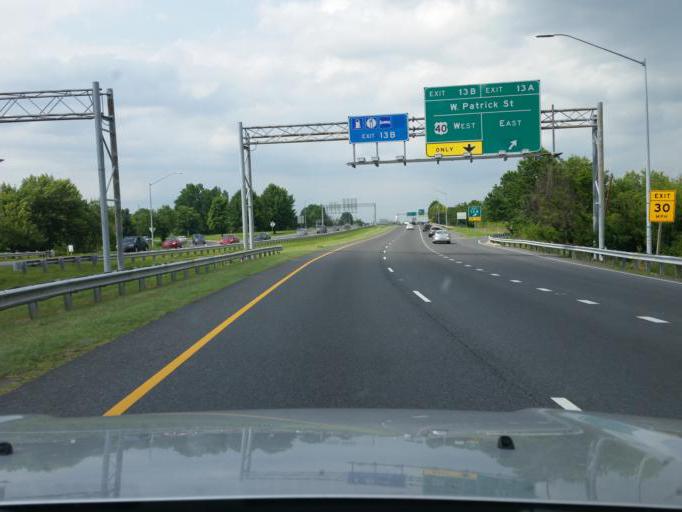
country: US
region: Maryland
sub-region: Frederick County
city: Frederick
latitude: 39.4121
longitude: -77.4358
